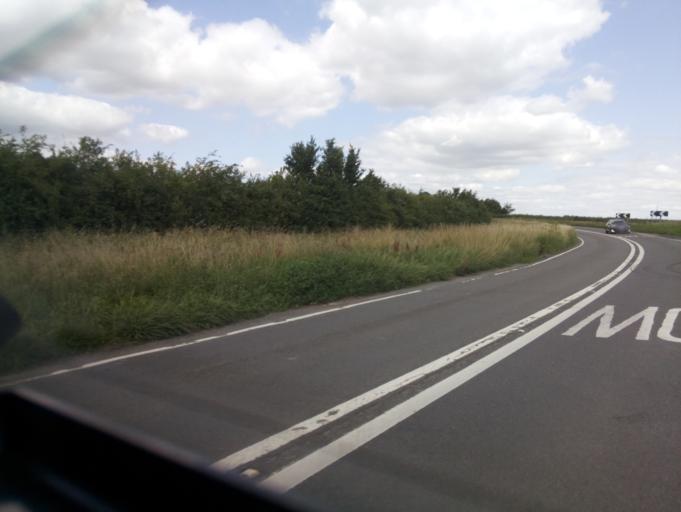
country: GB
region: England
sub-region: Buckinghamshire
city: Winslow
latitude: 51.9138
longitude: -0.8382
